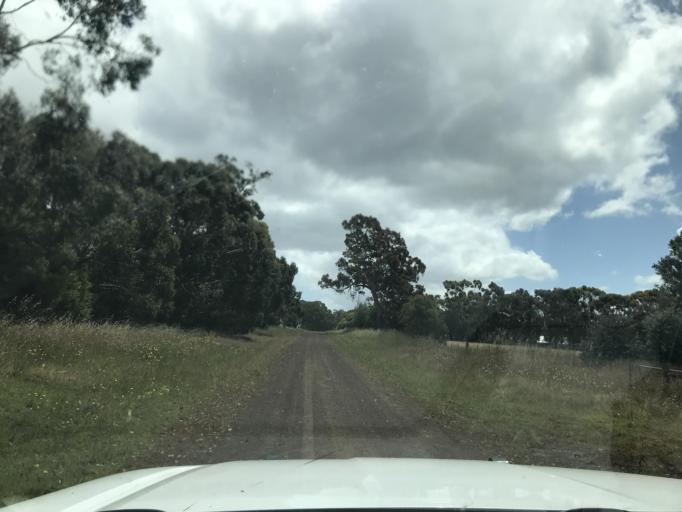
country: AU
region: South Australia
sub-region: Wattle Range
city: Penola
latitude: -37.2978
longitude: 141.4771
